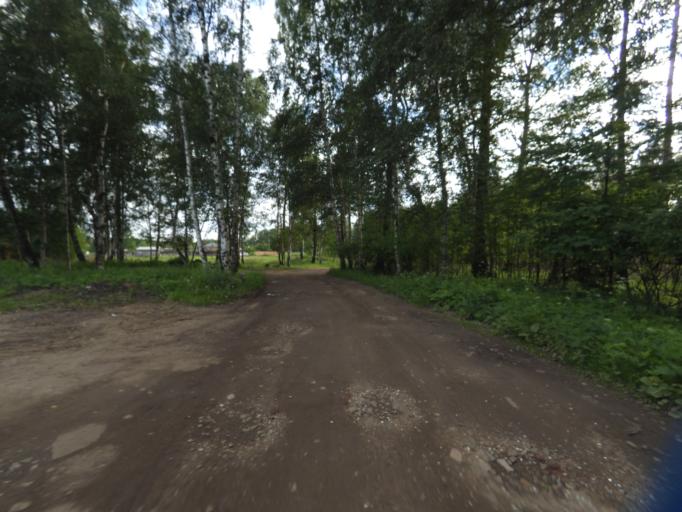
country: RU
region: Moskovskaya
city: Nekrasovskiy
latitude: 56.0743
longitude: 37.4963
